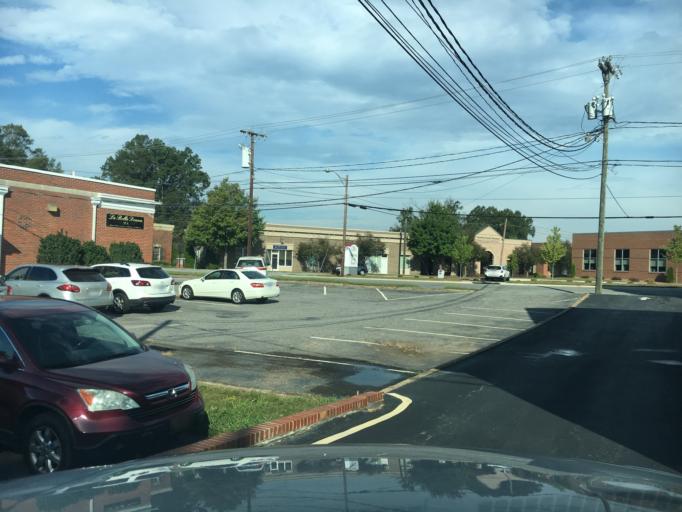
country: US
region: North Carolina
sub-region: Catawba County
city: Hickory
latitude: 35.7489
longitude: -81.3375
